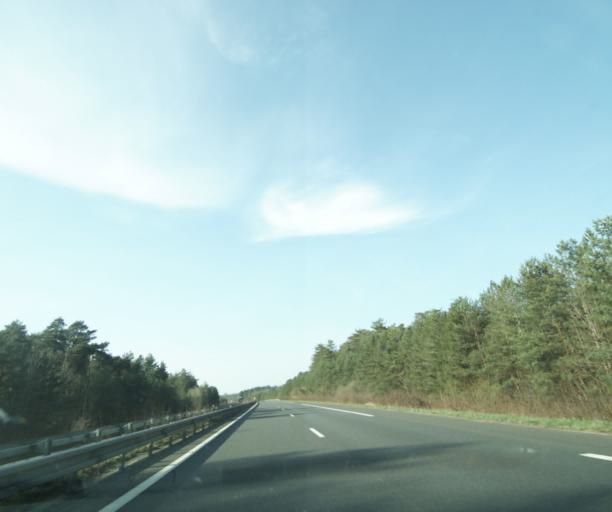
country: FR
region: Centre
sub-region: Departement du Loir-et-Cher
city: Lamotte-Beuvron
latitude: 47.5910
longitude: 1.9878
